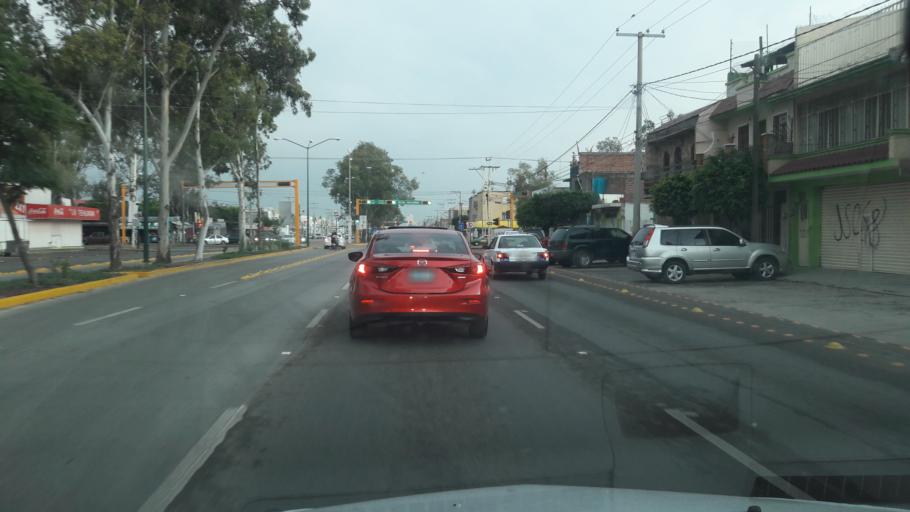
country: MX
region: Guanajuato
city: Leon
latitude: 21.1324
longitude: -101.6448
